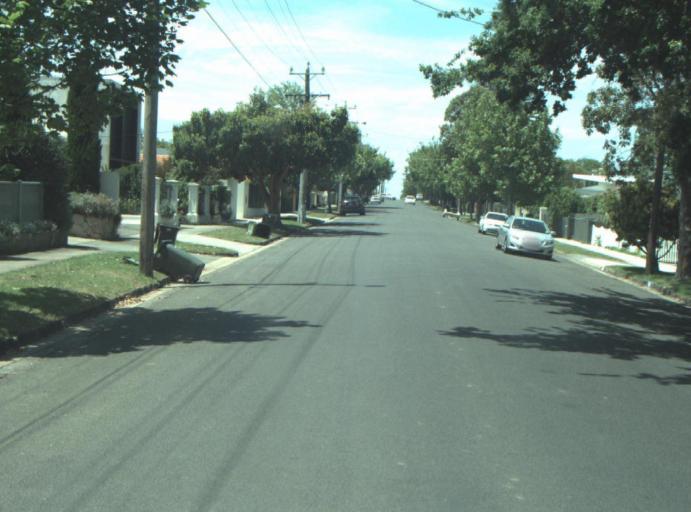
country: AU
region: Victoria
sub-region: Greater Geelong
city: Geelong West
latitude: -38.1519
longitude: 144.3281
